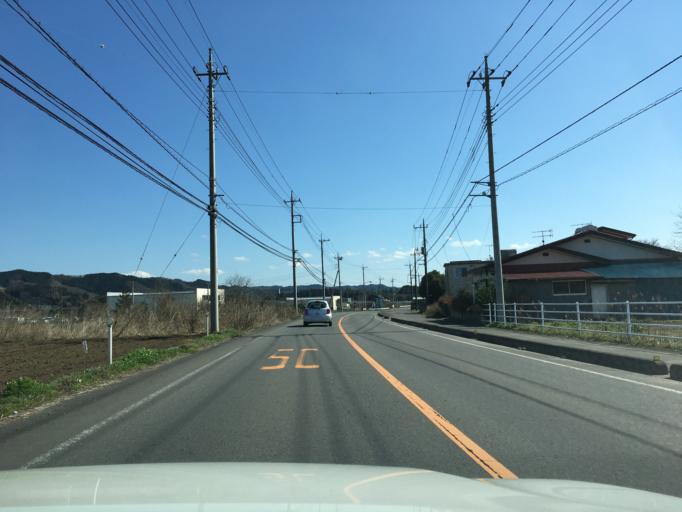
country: JP
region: Tochigi
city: Karasuyama
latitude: 36.7241
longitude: 140.1454
